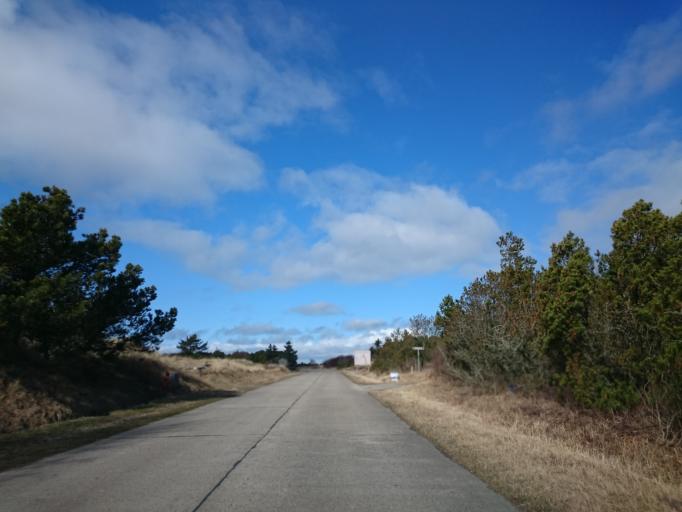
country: DK
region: North Denmark
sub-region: Frederikshavn Kommune
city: Skagen
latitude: 57.6563
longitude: 10.4149
